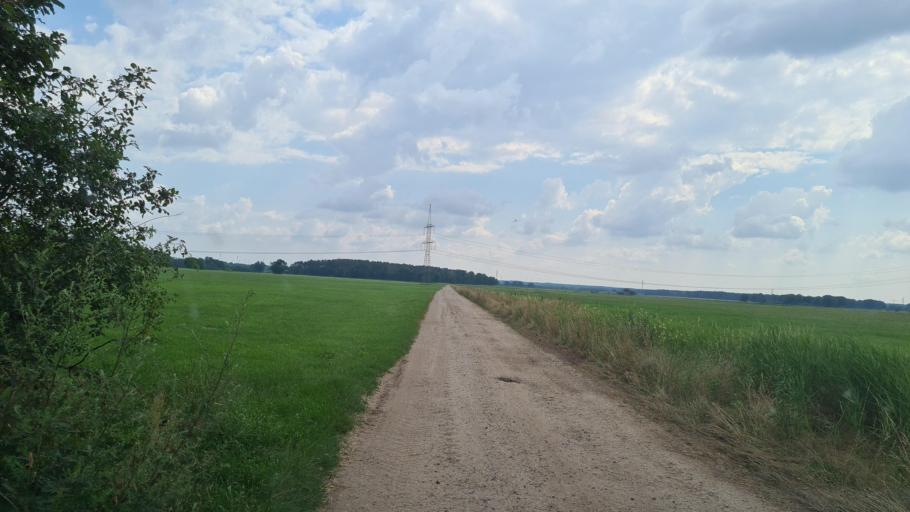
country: DE
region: Brandenburg
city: Sallgast
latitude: 51.6332
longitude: 13.8674
